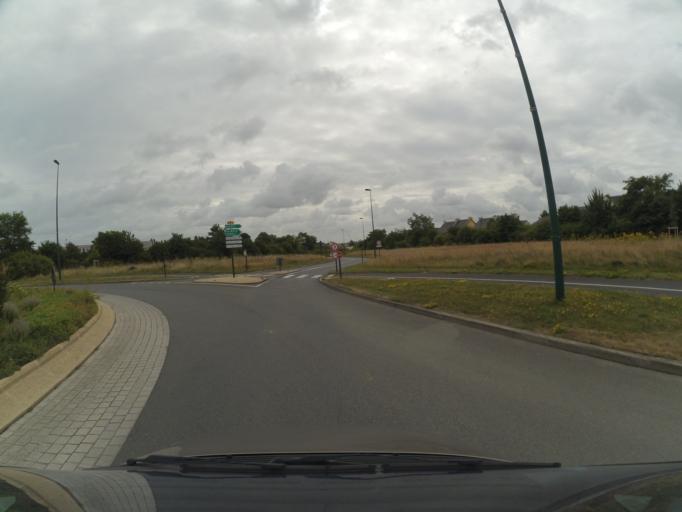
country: FR
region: Brittany
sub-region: Departement des Cotes-d'Armor
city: Ploufragan
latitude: 48.5152
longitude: -2.7942
